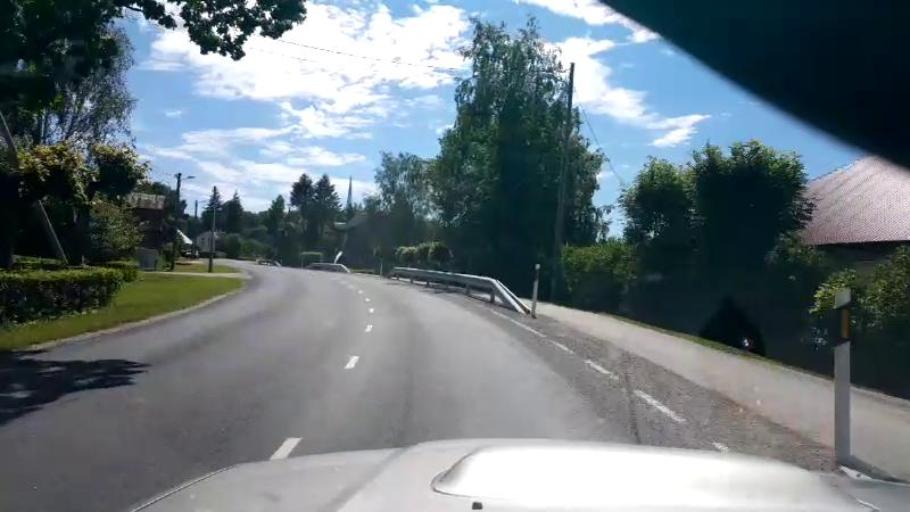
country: EE
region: Jaervamaa
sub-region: Jaerva-Jaani vald
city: Jarva-Jaani
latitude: 59.0435
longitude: 25.8823
